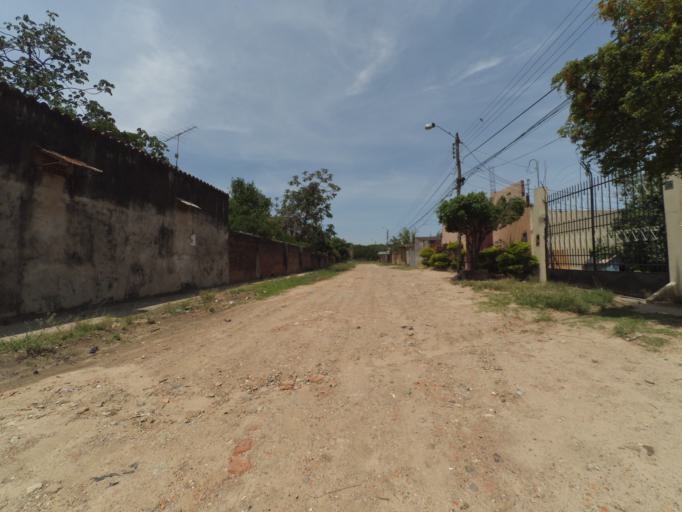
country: BO
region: Santa Cruz
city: Santa Cruz de la Sierra
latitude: -17.8233
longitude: -63.2237
